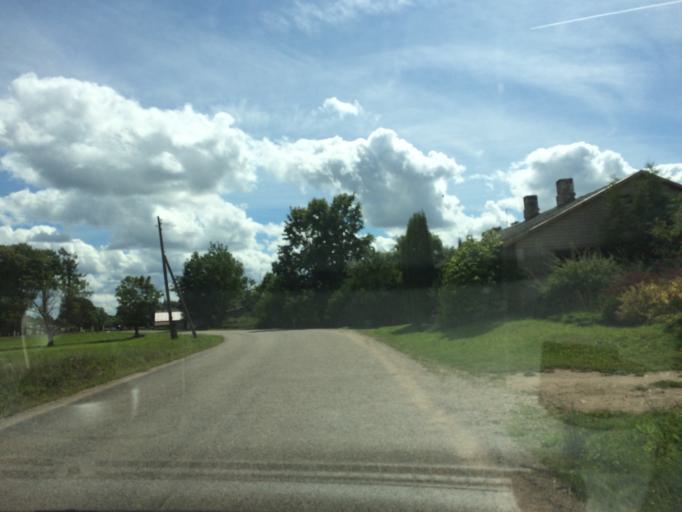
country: LV
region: Ludzas Rajons
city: Ludza
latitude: 56.6336
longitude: 27.5108
